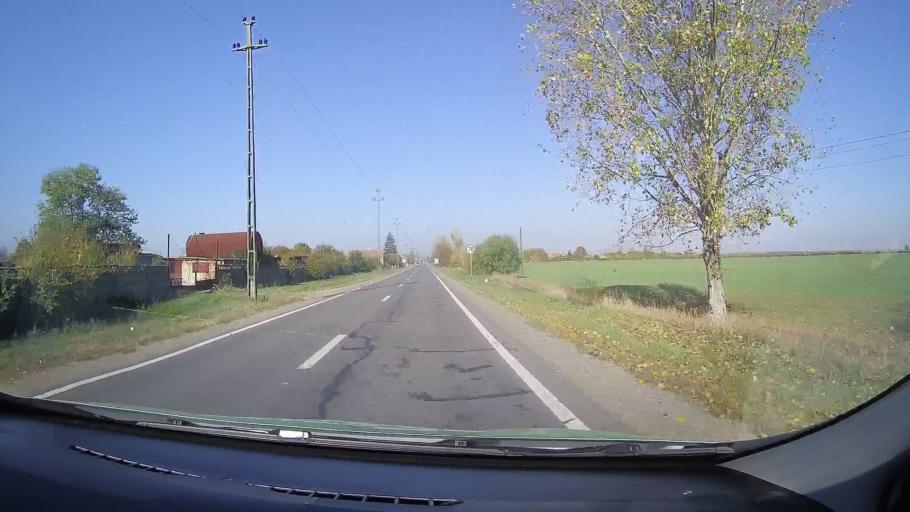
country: RO
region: Satu Mare
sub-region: Comuna Urziceni
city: Urziceni
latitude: 47.7244
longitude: 22.4121
